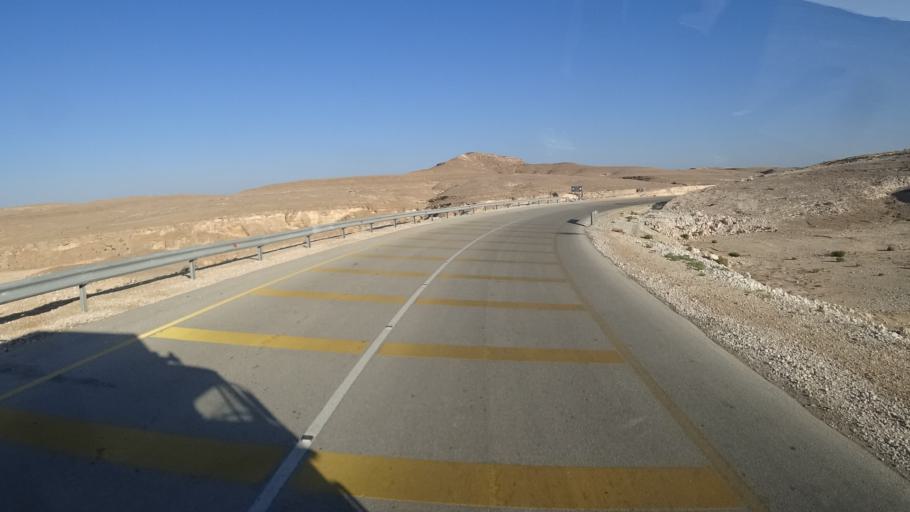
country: YE
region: Al Mahrah
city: Hawf
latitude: 17.0958
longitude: 53.0659
